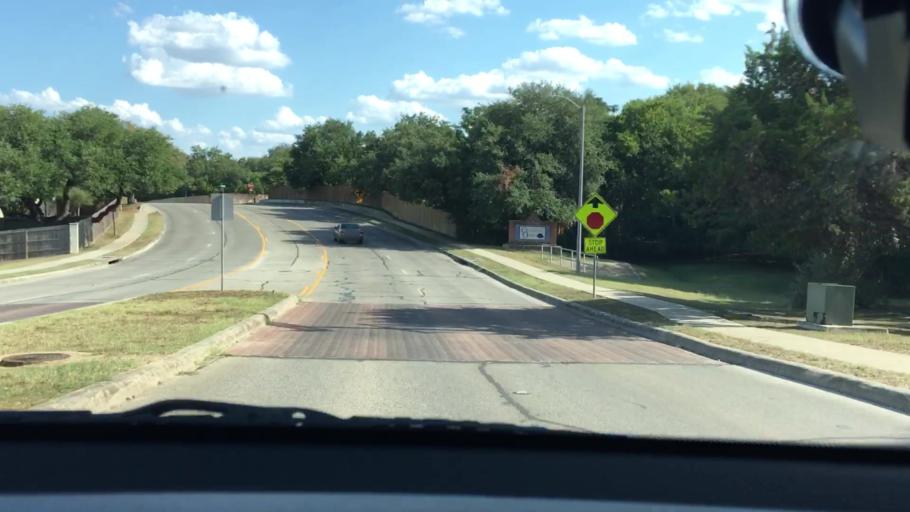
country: US
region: Texas
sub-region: Bexar County
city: Selma
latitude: 29.5624
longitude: -98.3128
